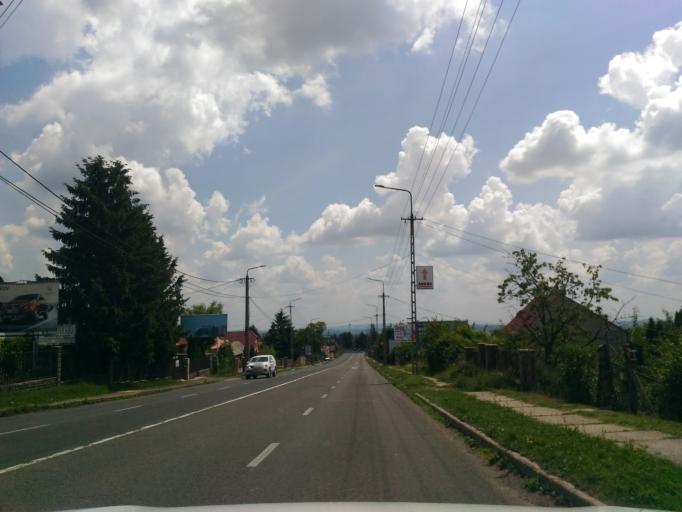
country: HU
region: Baranya
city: Pecs
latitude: 46.1151
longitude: 18.2616
